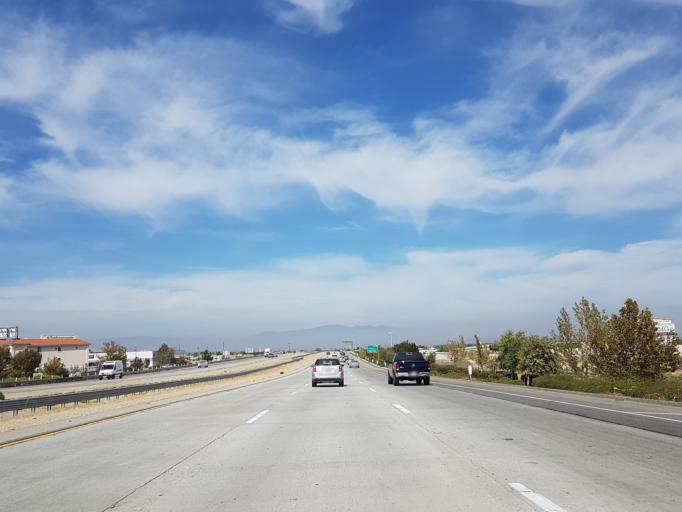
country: US
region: California
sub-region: Los Angeles County
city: Lancaster
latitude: 34.6781
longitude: -118.1603
